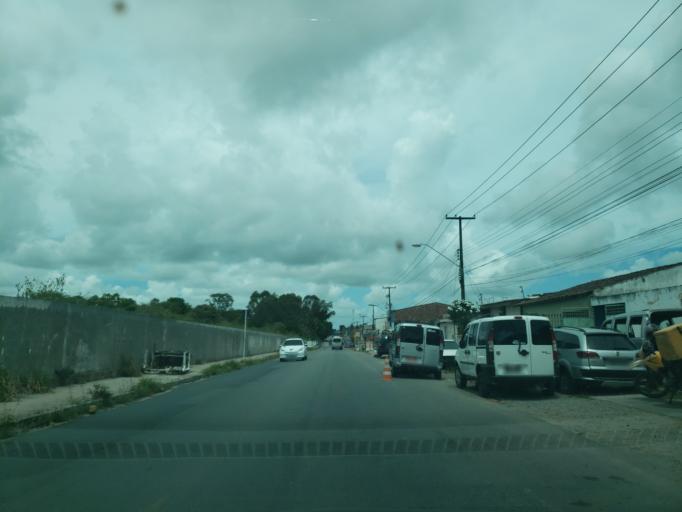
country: BR
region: Alagoas
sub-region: Satuba
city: Satuba
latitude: -9.5559
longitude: -35.7704
